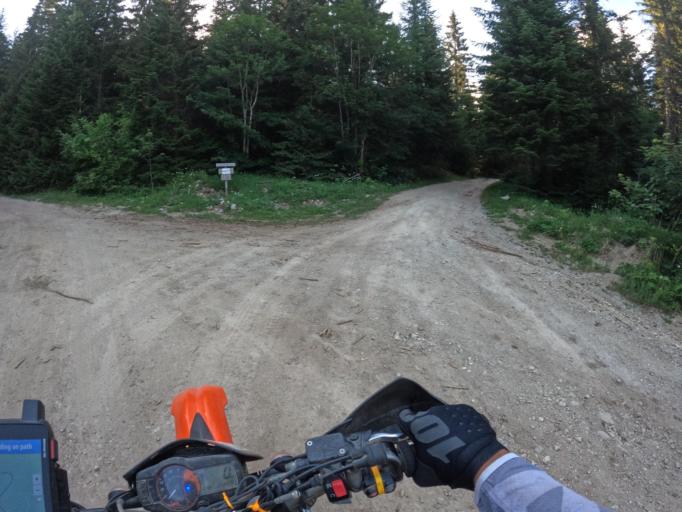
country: BA
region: Federation of Bosnia and Herzegovina
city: Glamoc
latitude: 44.0219
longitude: 16.7887
